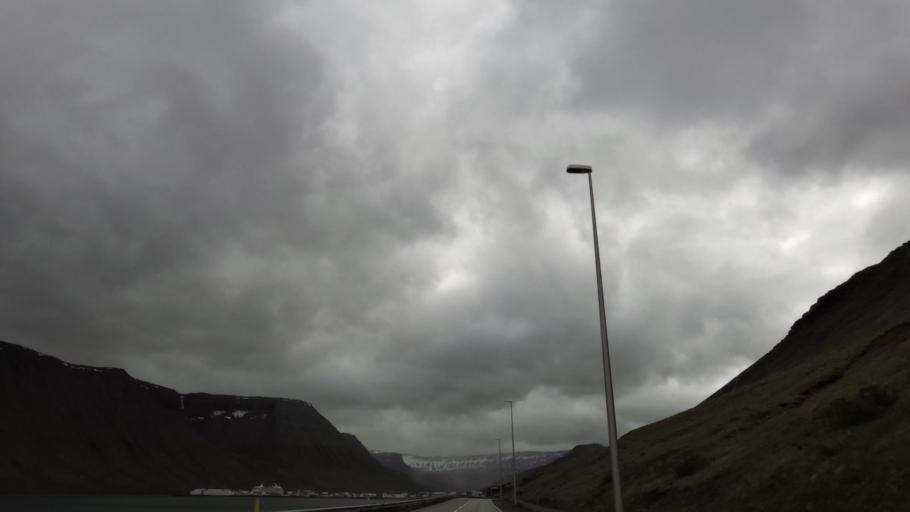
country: IS
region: Westfjords
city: Isafjoerdur
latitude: 66.0889
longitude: -23.1170
